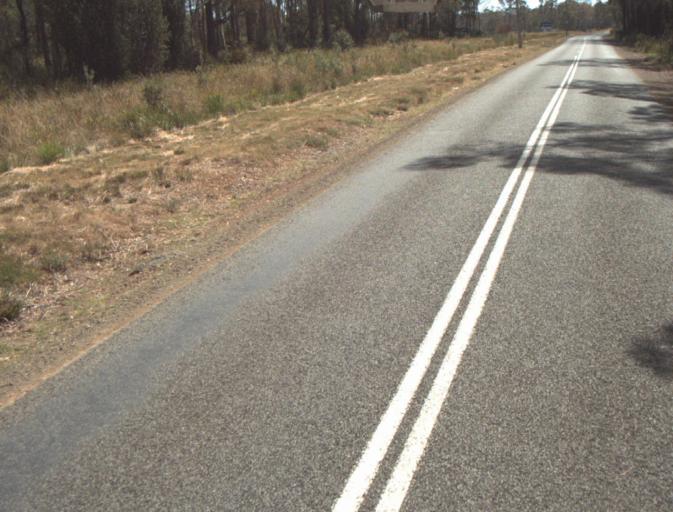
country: AU
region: Tasmania
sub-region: Launceston
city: Mayfield
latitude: -41.3256
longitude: 147.1381
